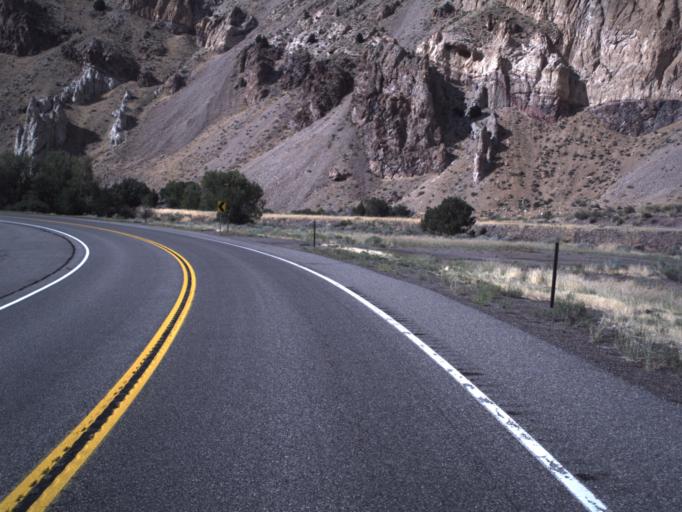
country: US
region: Utah
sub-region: Sevier County
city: Monroe
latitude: 38.5698
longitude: -112.2527
